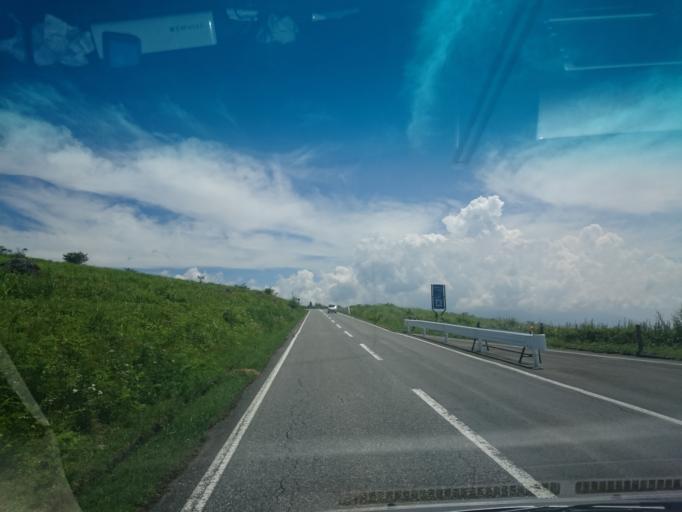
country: JP
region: Nagano
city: Suwa
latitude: 36.0963
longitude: 138.1718
